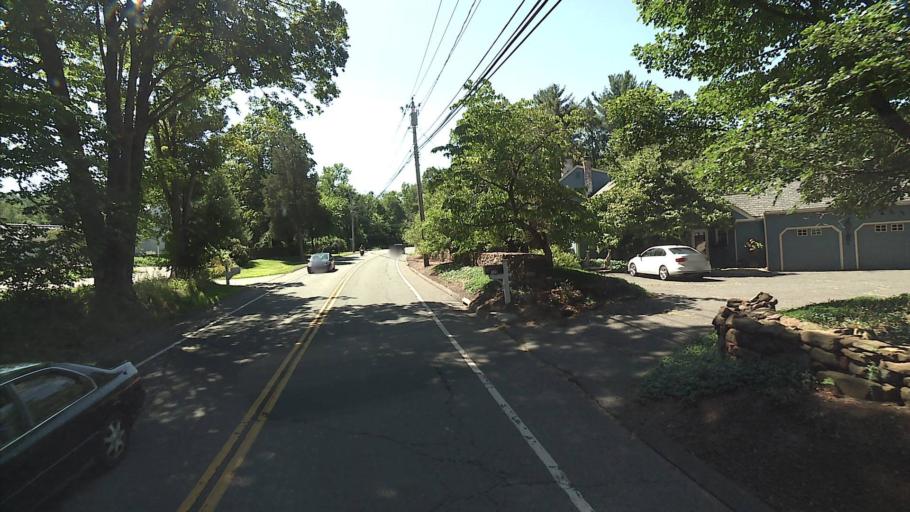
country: US
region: Connecticut
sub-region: Hartford County
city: Weatogue
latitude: 41.7925
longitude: -72.8158
